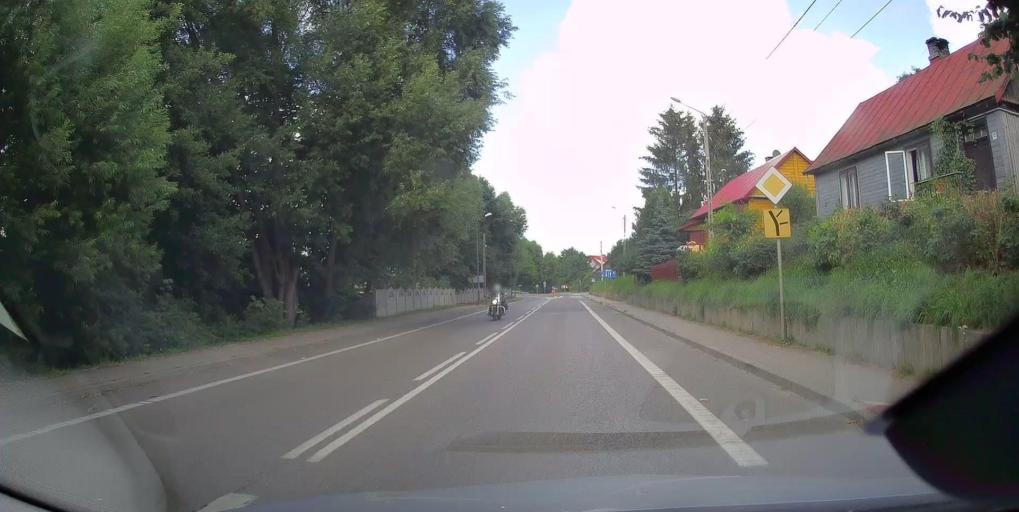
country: PL
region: Swietokrzyskie
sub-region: Powiat kielecki
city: Nowa Slupia
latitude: 50.8613
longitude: 21.0900
